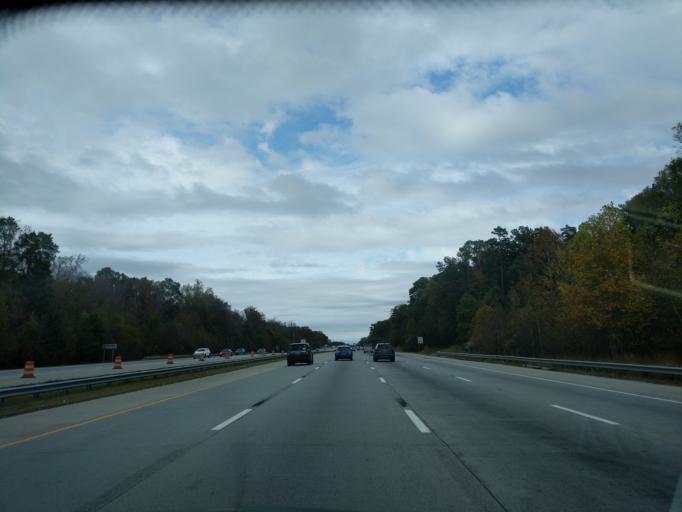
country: US
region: North Carolina
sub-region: Rowan County
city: China Grove
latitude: 35.5876
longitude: -80.5457
